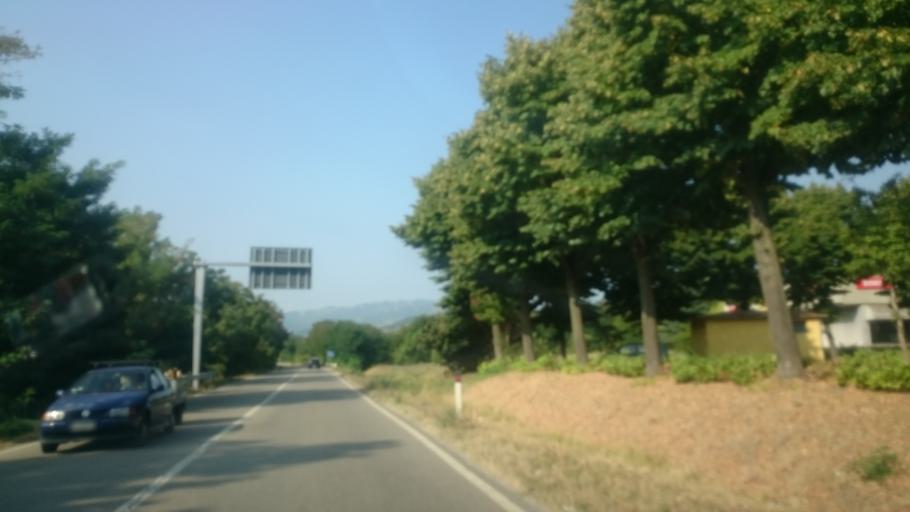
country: IT
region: Emilia-Romagna
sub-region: Provincia di Reggio Emilia
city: Roteglia
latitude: 44.4874
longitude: 10.6936
